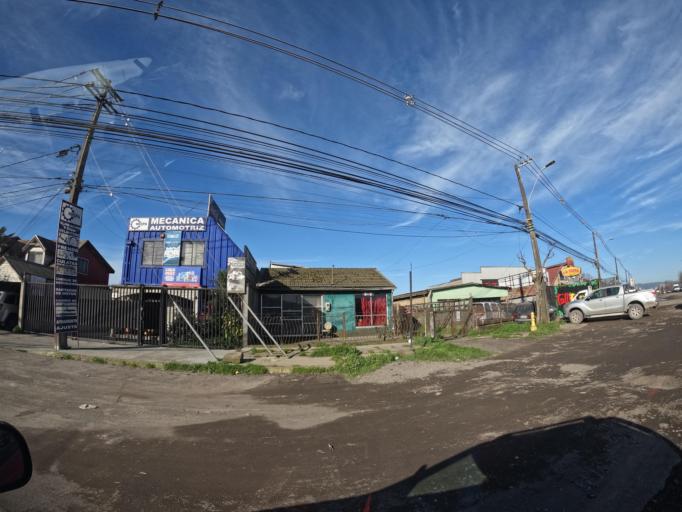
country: CL
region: Biobio
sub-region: Provincia de Concepcion
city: Talcahuano
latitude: -36.7713
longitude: -73.0822
